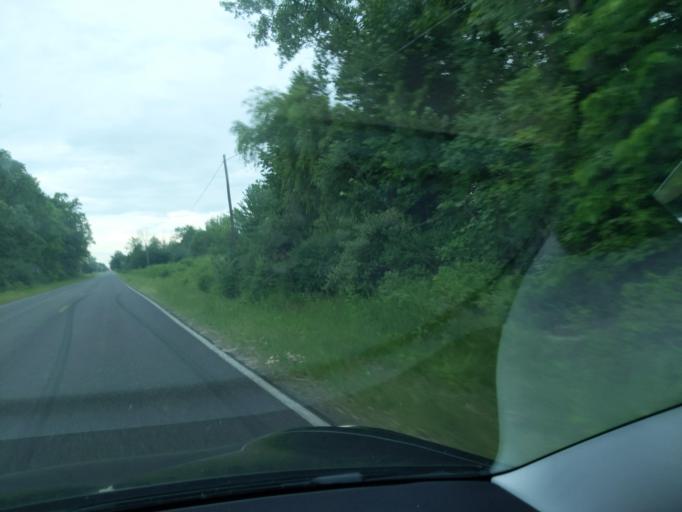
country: US
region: Michigan
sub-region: Isabella County
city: Mount Pleasant
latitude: 43.6175
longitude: -84.7279
